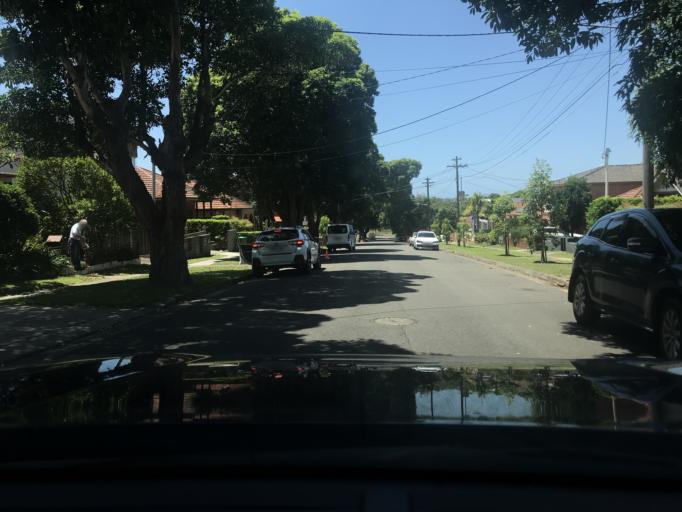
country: AU
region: New South Wales
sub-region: Canada Bay
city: Concord
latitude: -33.8596
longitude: 151.1004
